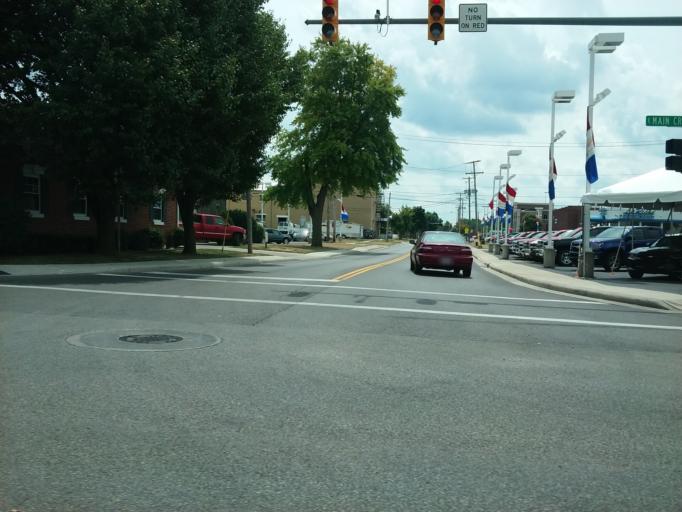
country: US
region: Ohio
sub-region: Hancock County
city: Findlay
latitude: 41.0391
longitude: -83.6469
